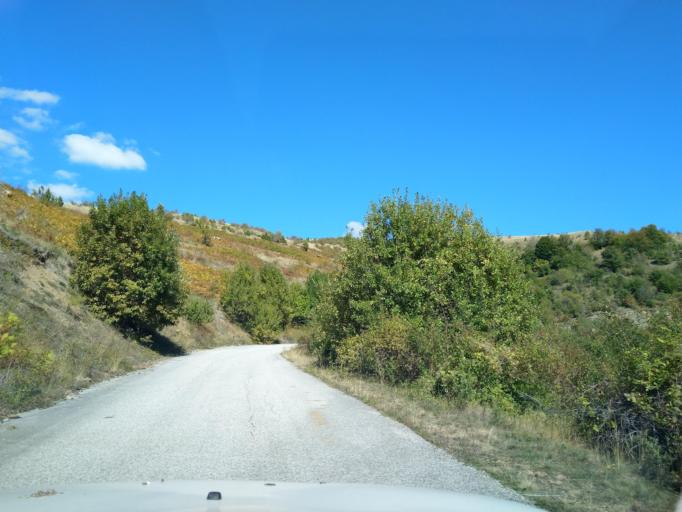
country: RS
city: Sokolovica
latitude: 43.2546
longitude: 20.3333
